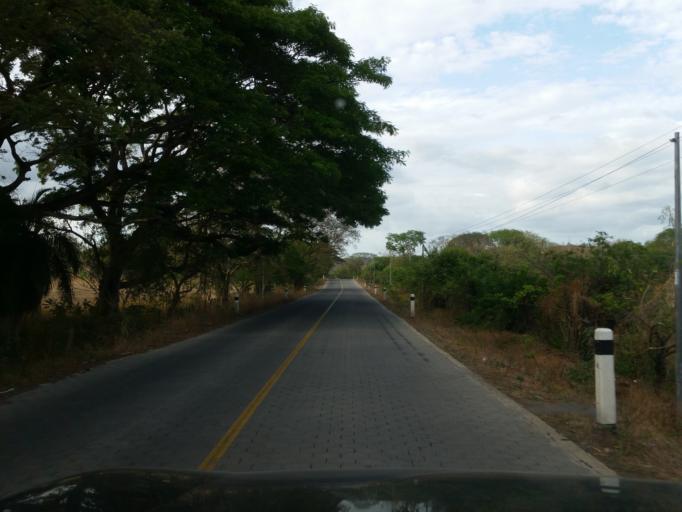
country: NI
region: Rivas
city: Tola
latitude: 11.4260
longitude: -85.9460
